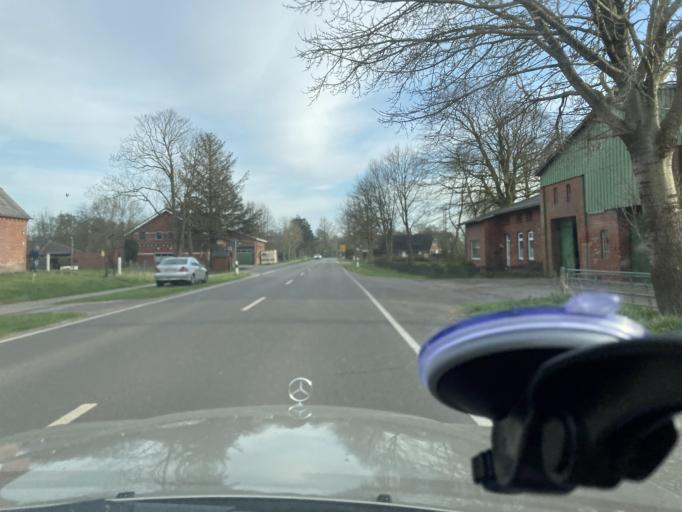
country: DE
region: Schleswig-Holstein
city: Stelle-Wittenwurth
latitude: 54.2744
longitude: 9.0471
